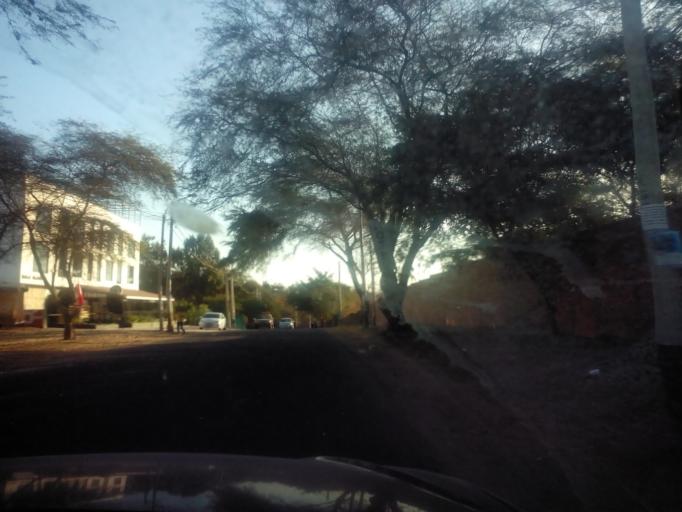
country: PE
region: Ica
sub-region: Provincia de Ica
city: Subtanjalla
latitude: -14.0488
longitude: -75.7527
